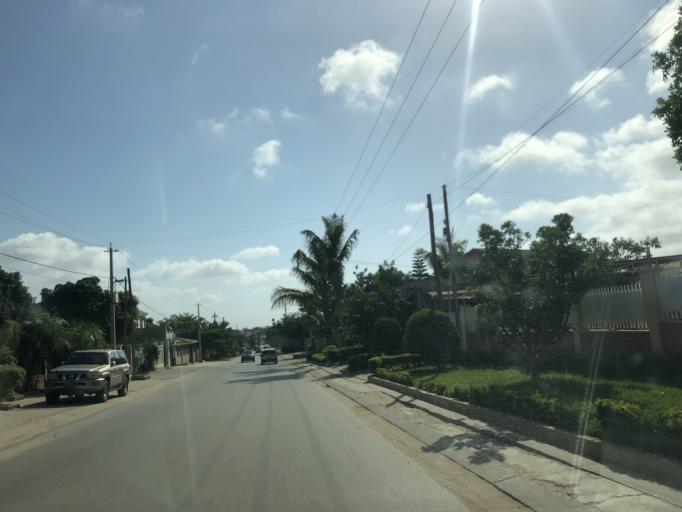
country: AO
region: Luanda
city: Luanda
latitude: -8.9077
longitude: 13.2301
